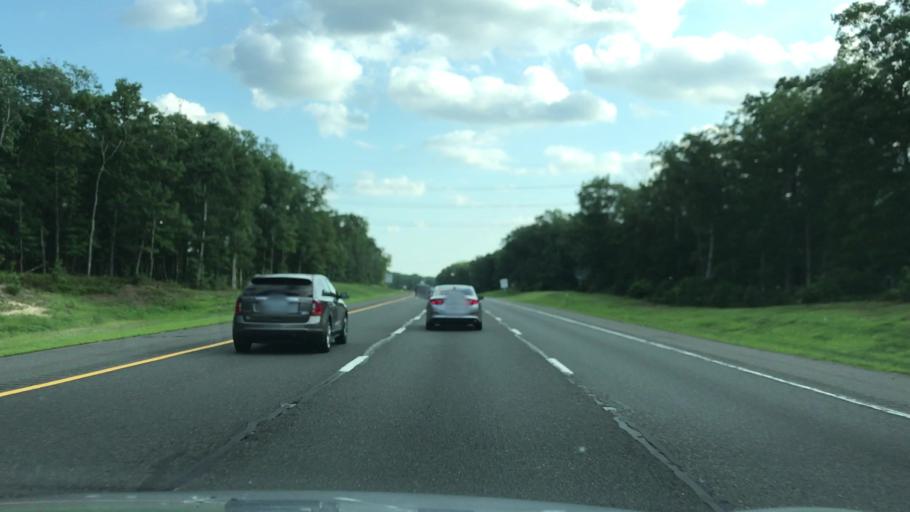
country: US
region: New Jersey
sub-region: Ocean County
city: Ocean Acres
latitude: 39.7469
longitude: -74.2564
